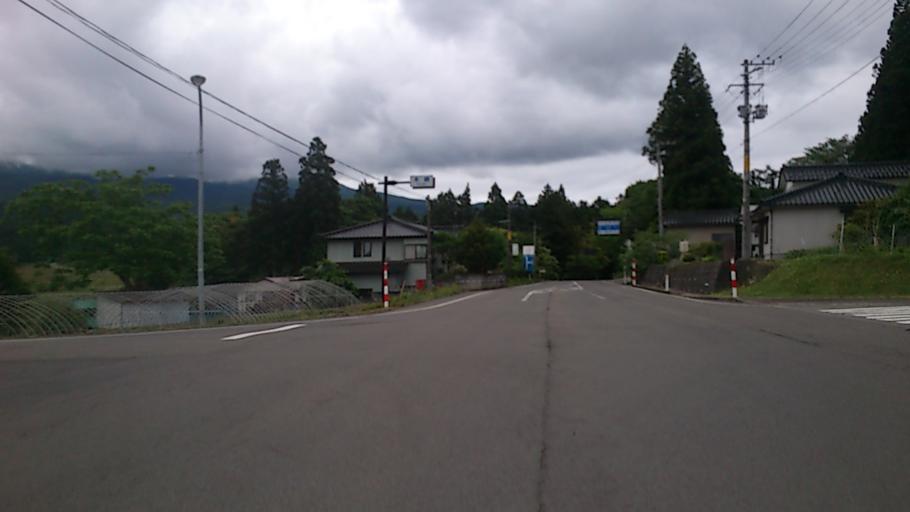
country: JP
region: Yamagata
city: Yuza
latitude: 39.1741
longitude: 139.9483
